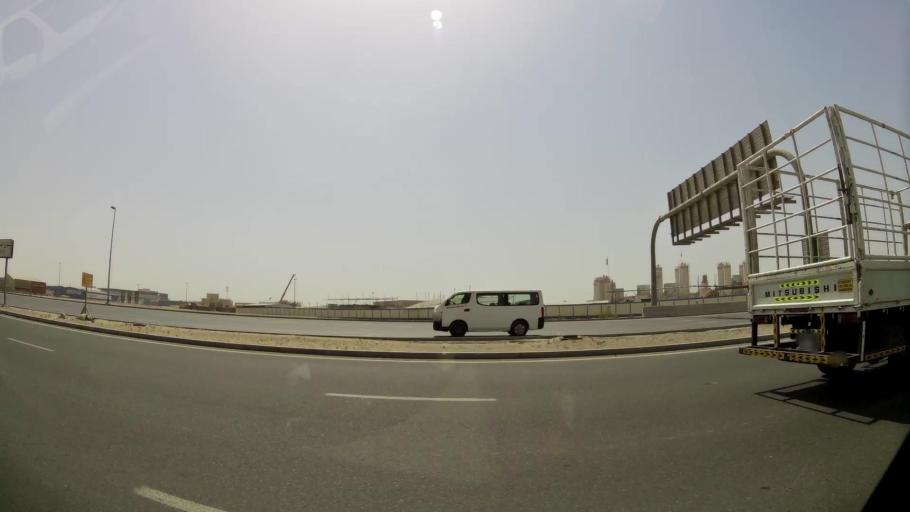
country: AE
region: Dubai
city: Dubai
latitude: 25.1568
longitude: 55.2367
